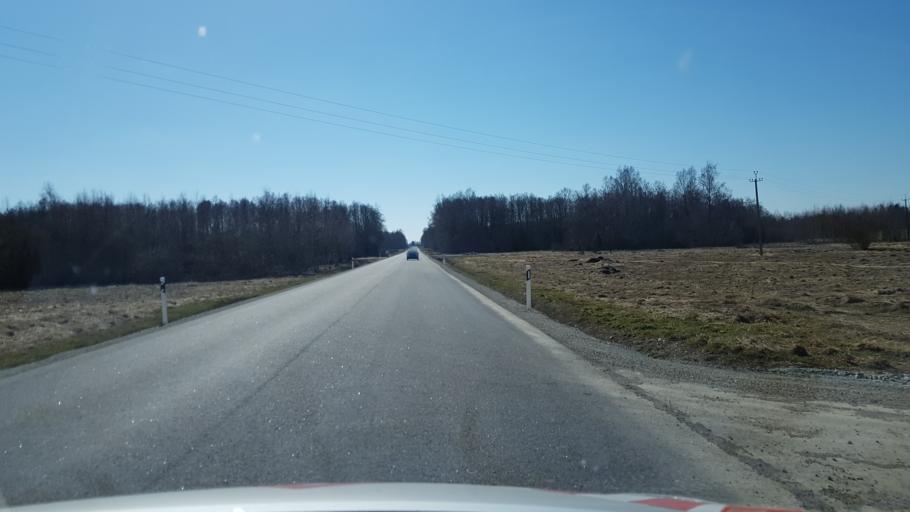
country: EE
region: Laeaene-Virumaa
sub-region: Vinni vald
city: Vinni
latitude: 59.0989
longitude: 26.6208
